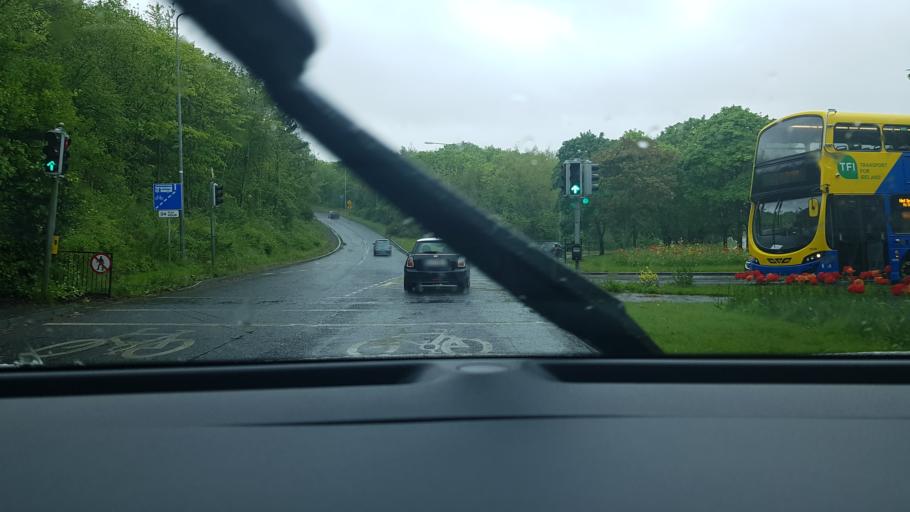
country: IE
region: Leinster
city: Ballyfermot
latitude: 53.3481
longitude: -6.3532
